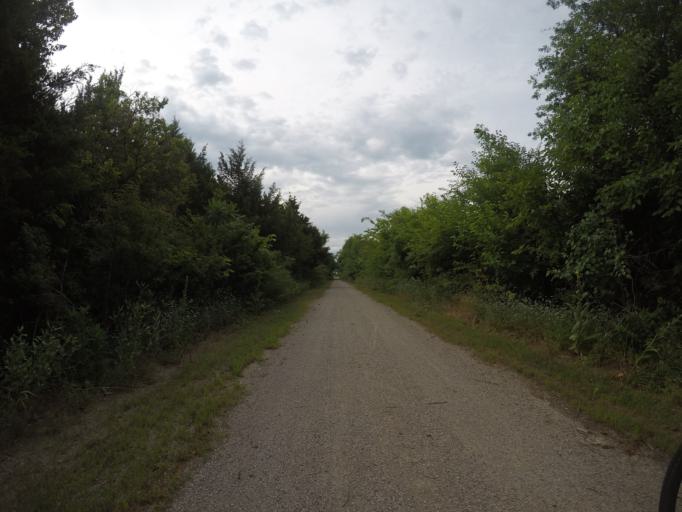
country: US
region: Kansas
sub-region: Franklin County
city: Ottawa
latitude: 38.4538
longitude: -95.2680
